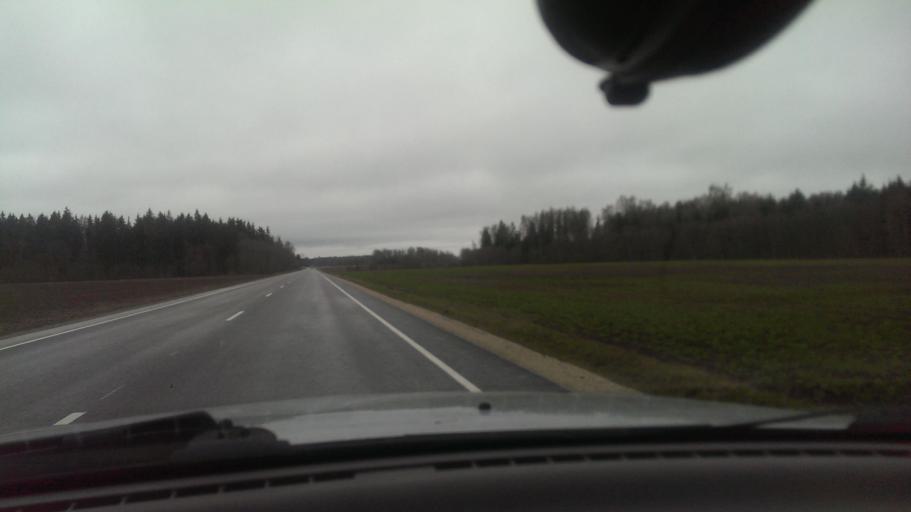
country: EE
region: Tartu
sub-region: Tartu linn
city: Tartu
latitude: 58.3874
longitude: 26.8896
